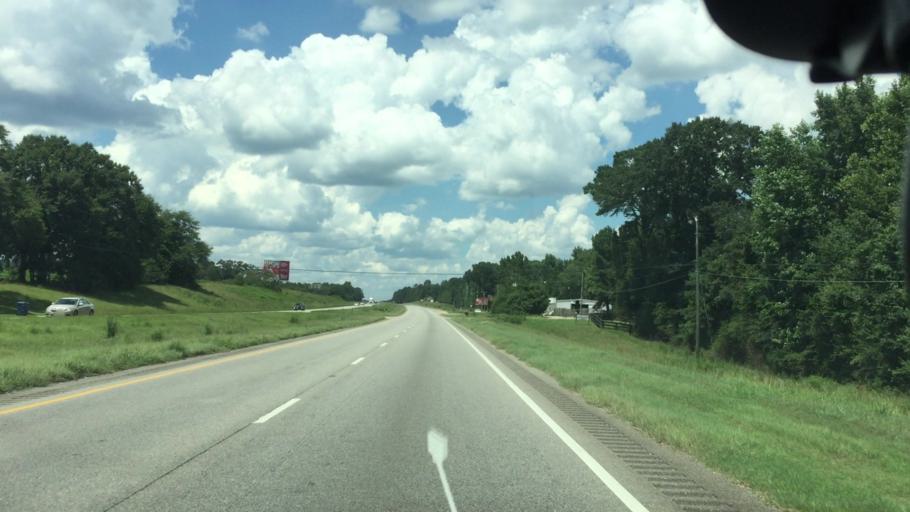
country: US
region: Alabama
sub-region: Pike County
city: Troy
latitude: 31.8678
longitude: -86.0000
